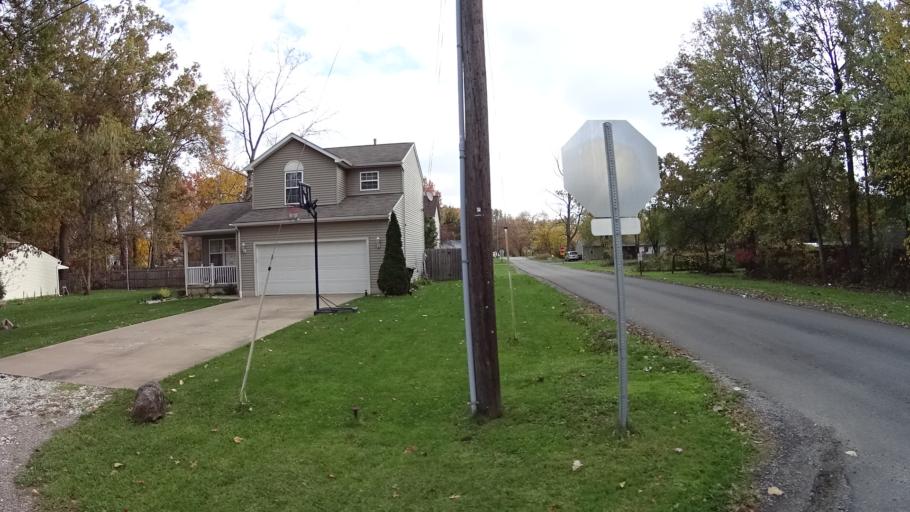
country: US
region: Ohio
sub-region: Lorain County
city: Sheffield
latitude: 41.4227
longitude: -82.1160
